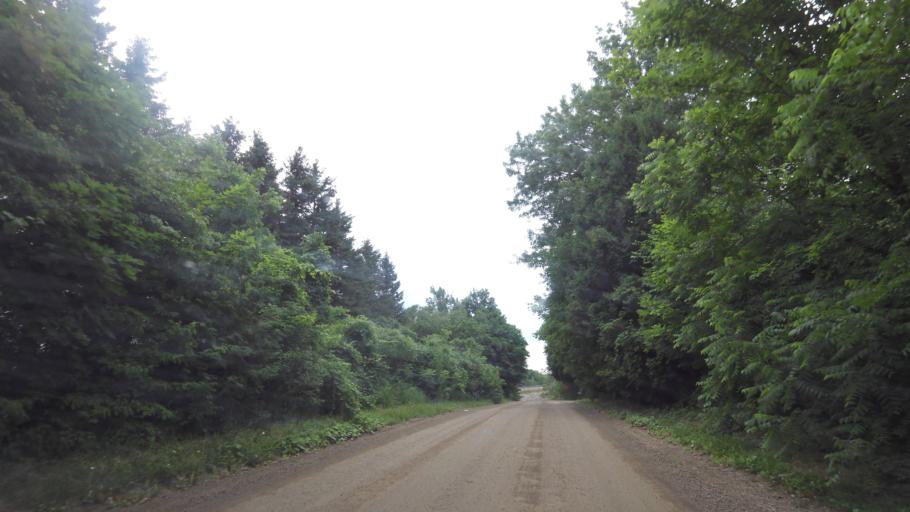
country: CA
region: Ontario
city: Orangeville
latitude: 43.8420
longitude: -79.9675
